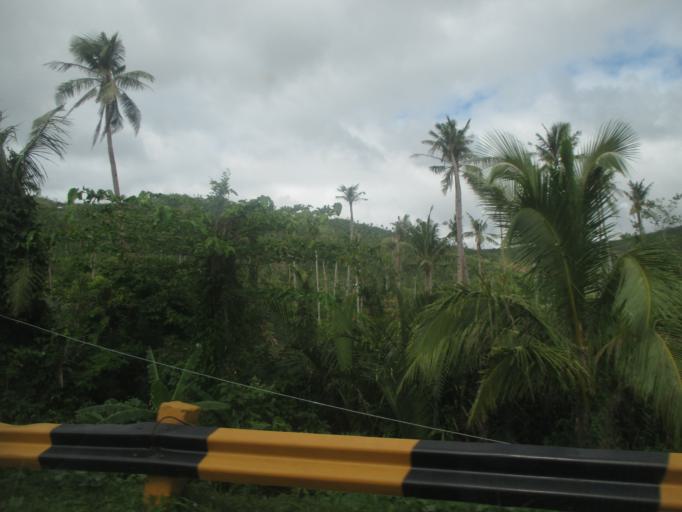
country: PH
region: Eastern Visayas
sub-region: Province of Eastern Samar
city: Lawa-an
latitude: 11.1287
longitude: 125.2586
